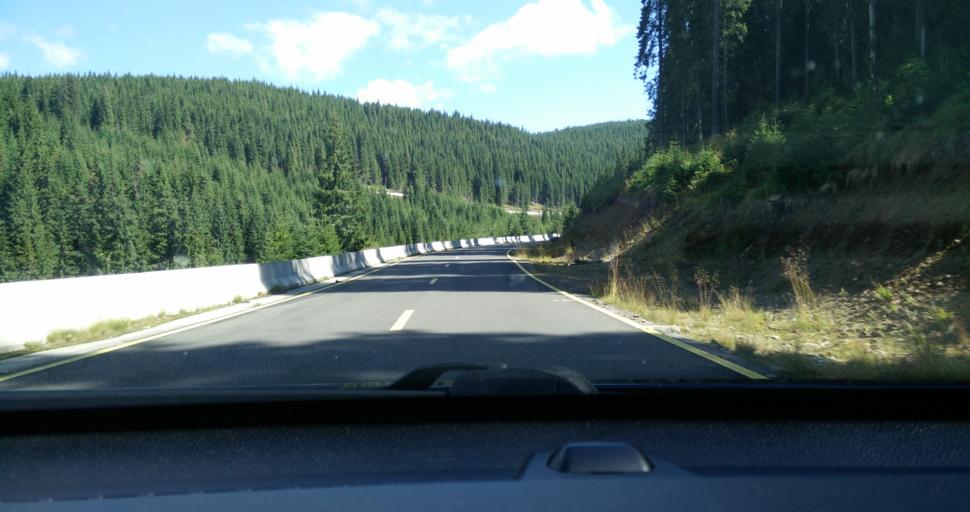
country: RO
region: Hunedoara
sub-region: Oras Petrila
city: Petrila
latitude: 45.4595
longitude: 23.6165
